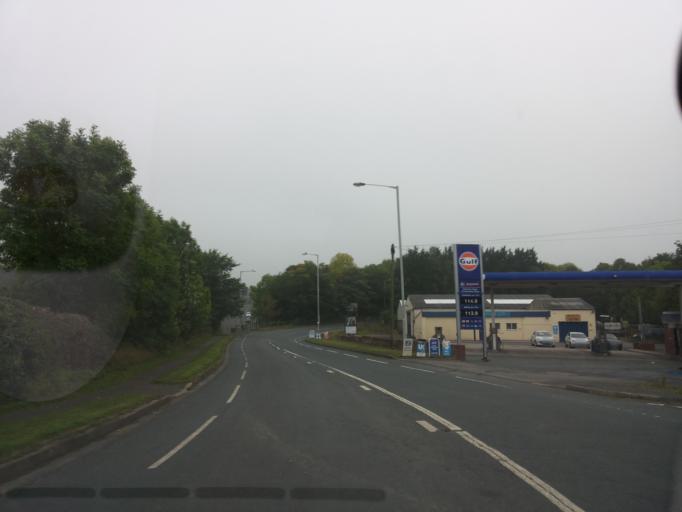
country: GB
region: England
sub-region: Lancashire
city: Langho
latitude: 53.8095
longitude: -2.4411
